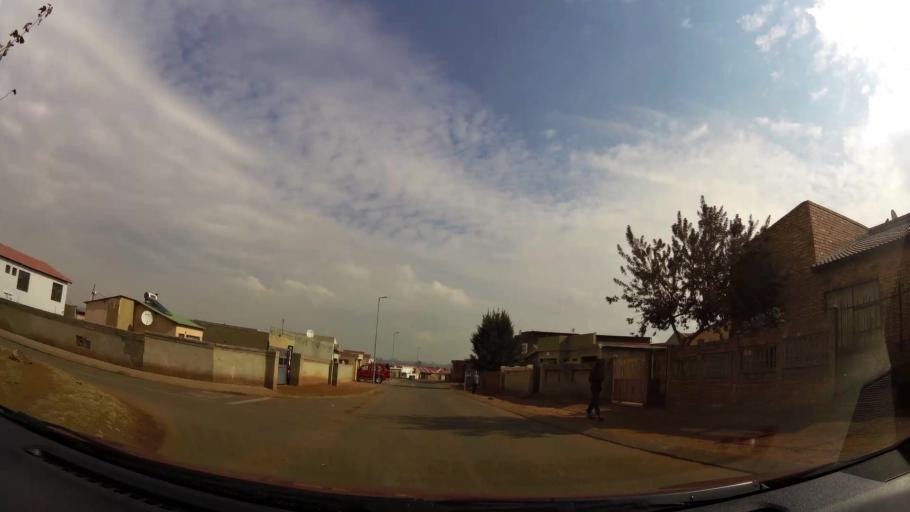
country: ZA
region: Gauteng
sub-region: City of Johannesburg Metropolitan Municipality
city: Soweto
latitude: -26.2584
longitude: 27.8177
